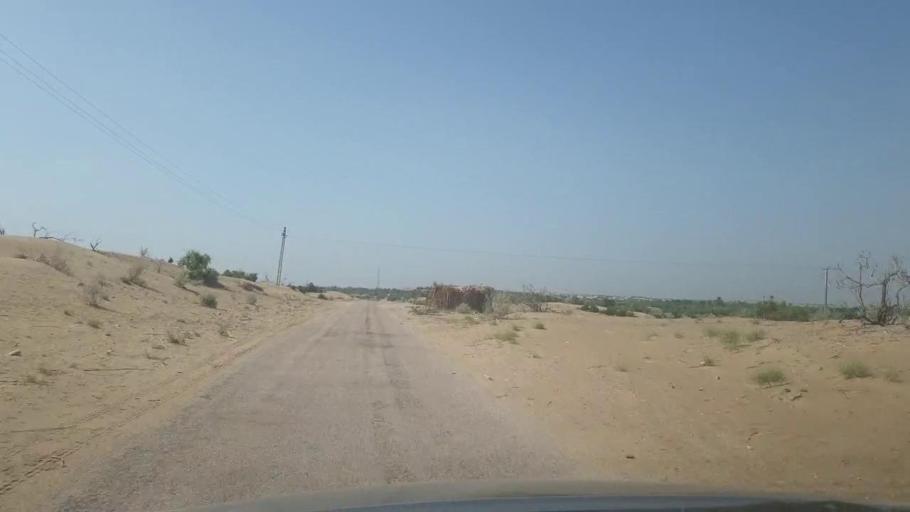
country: PK
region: Sindh
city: Rohri
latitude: 27.4232
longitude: 69.0796
